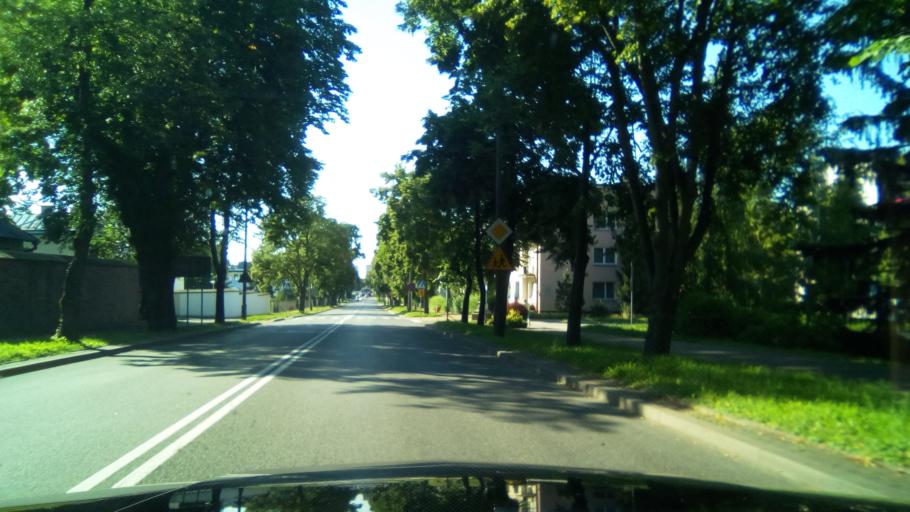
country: PL
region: Lublin Voivodeship
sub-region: Powiat pulawski
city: Pulawy
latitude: 51.4140
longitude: 21.9614
